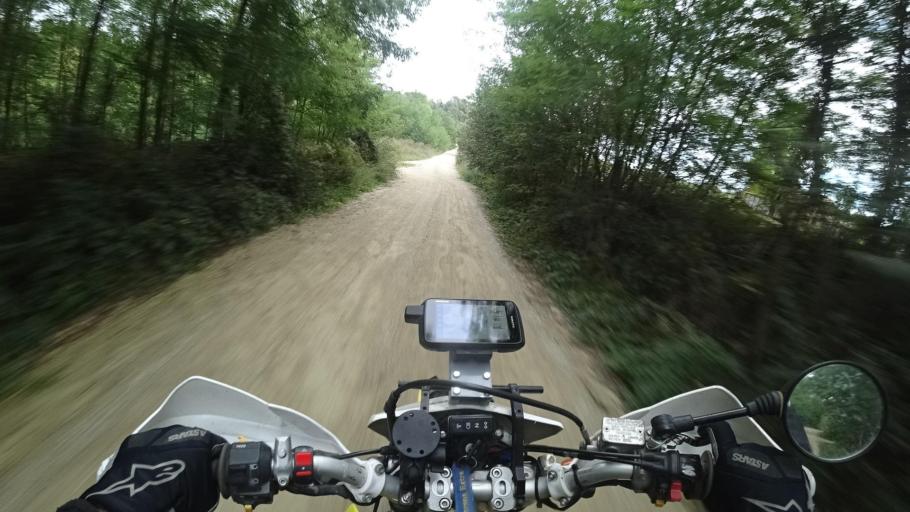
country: BA
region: Republika Srpska
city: Svodna
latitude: 45.0829
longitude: 16.5659
